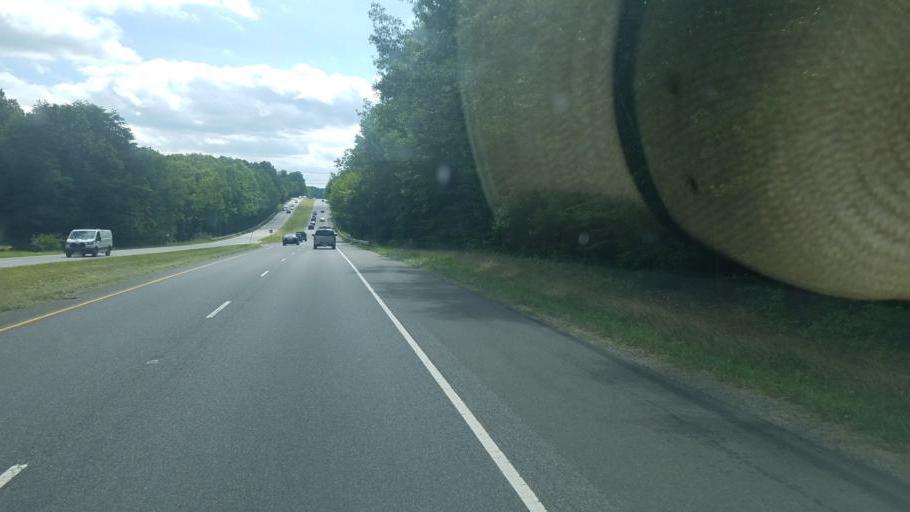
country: US
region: Virginia
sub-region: Stafford County
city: Falmouth
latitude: 38.4090
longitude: -77.5980
